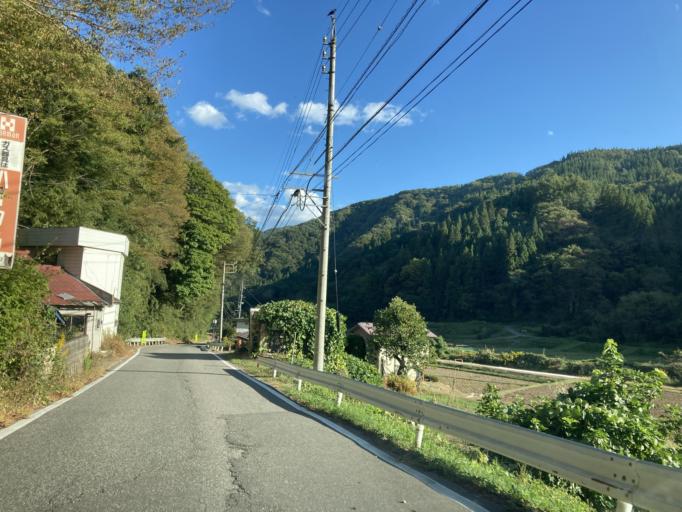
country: JP
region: Nagano
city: Omachi
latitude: 36.4727
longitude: 137.9355
